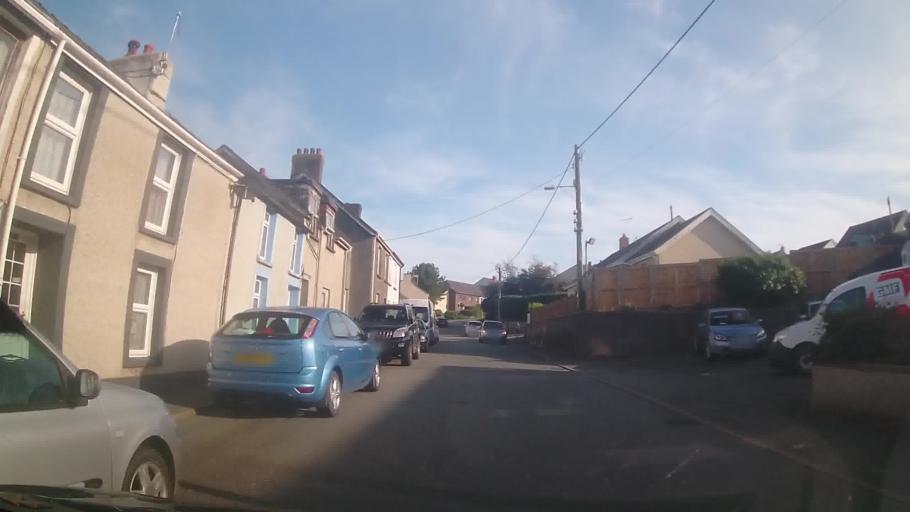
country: GB
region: Wales
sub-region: Pembrokeshire
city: Fishguard
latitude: 51.9928
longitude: -4.9728
